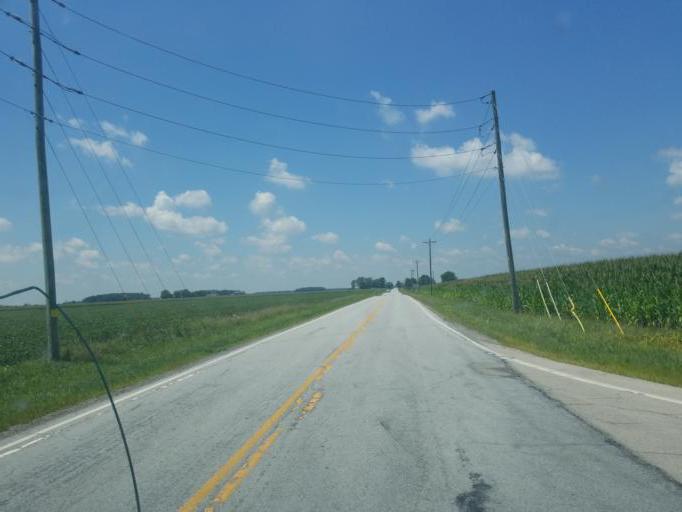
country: US
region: Ohio
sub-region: Allen County
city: Spencerville
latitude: 40.7140
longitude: -84.4161
